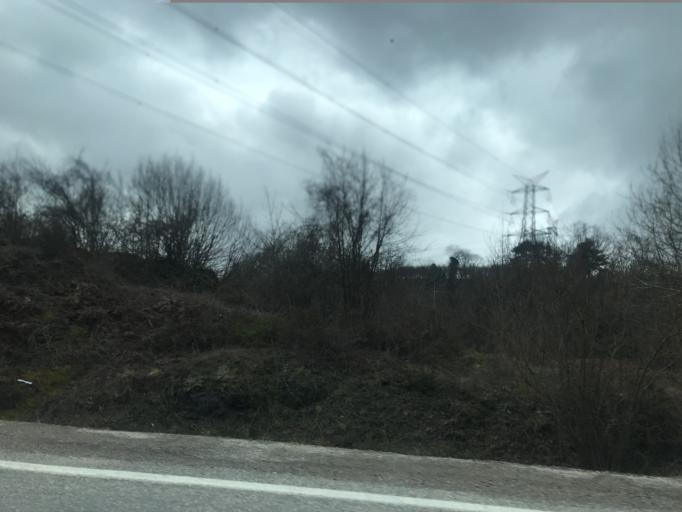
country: TR
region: Bartin
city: Amasra
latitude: 41.7111
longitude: 32.3918
